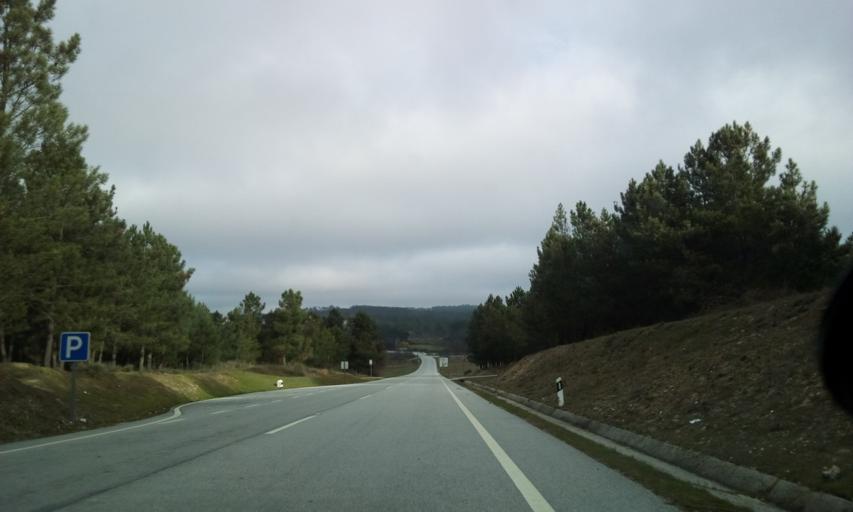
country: PT
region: Guarda
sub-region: Fornos de Algodres
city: Fornos de Algodres
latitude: 40.7137
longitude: -7.4866
